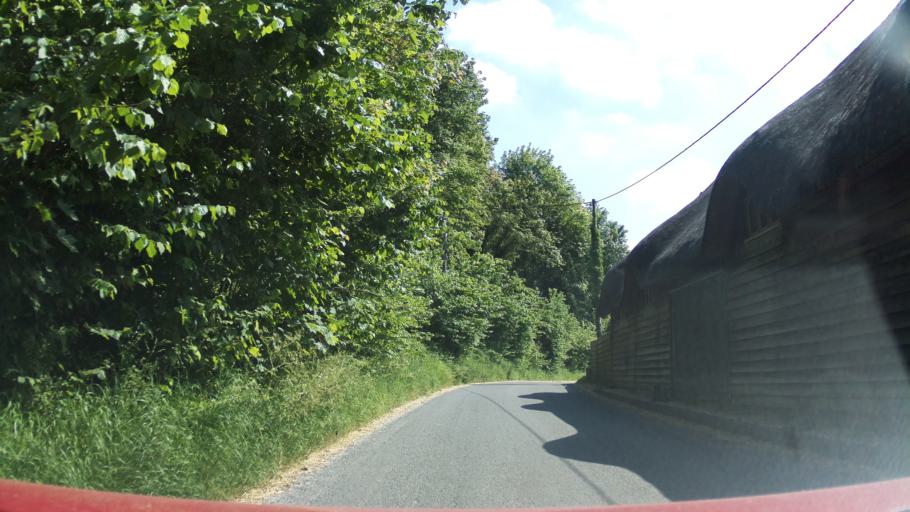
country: GB
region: England
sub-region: Wiltshire
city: Rushall
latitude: 51.2646
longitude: -1.7965
